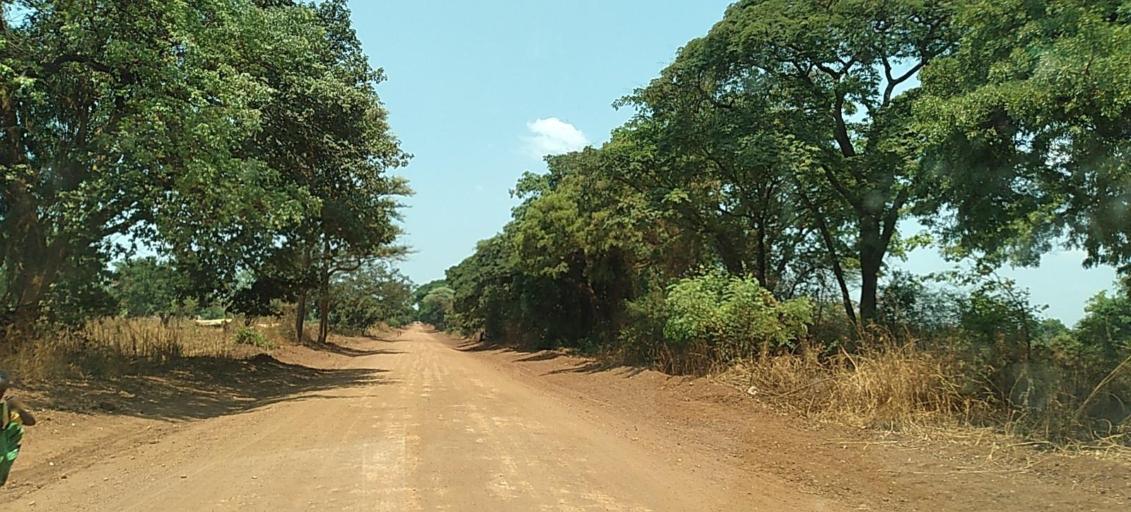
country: ZM
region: Copperbelt
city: Mpongwe
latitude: -13.5158
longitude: 28.0061
